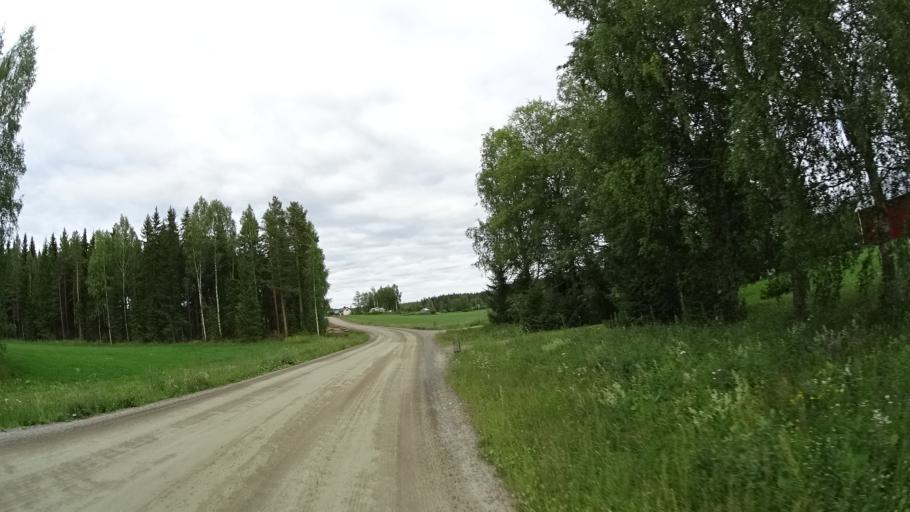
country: FI
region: Satakunta
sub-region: Pohjois-Satakunta
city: Jaemijaervi
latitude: 61.7678
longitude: 22.8361
